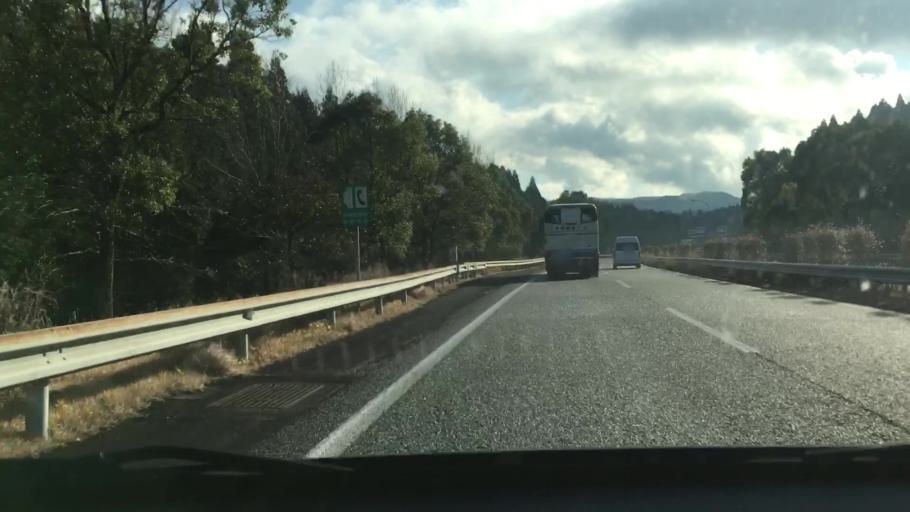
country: JP
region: Kagoshima
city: Okuchi-shinohara
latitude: 32.0317
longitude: 130.7980
